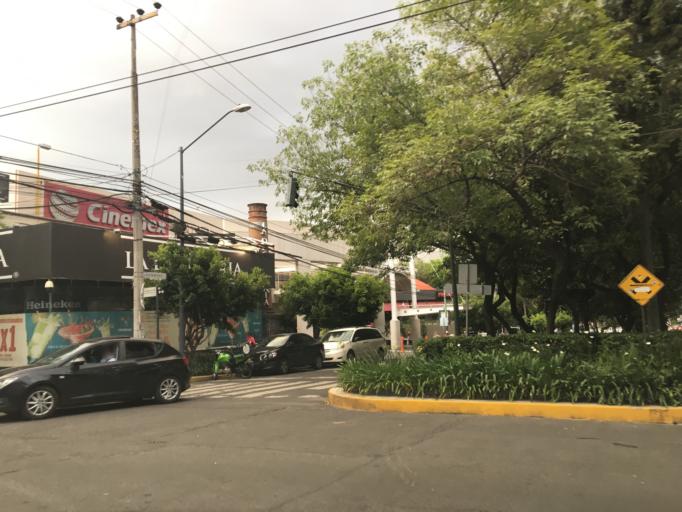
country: MX
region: Mexico City
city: Miguel Hidalgo
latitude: 19.4365
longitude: -99.2081
